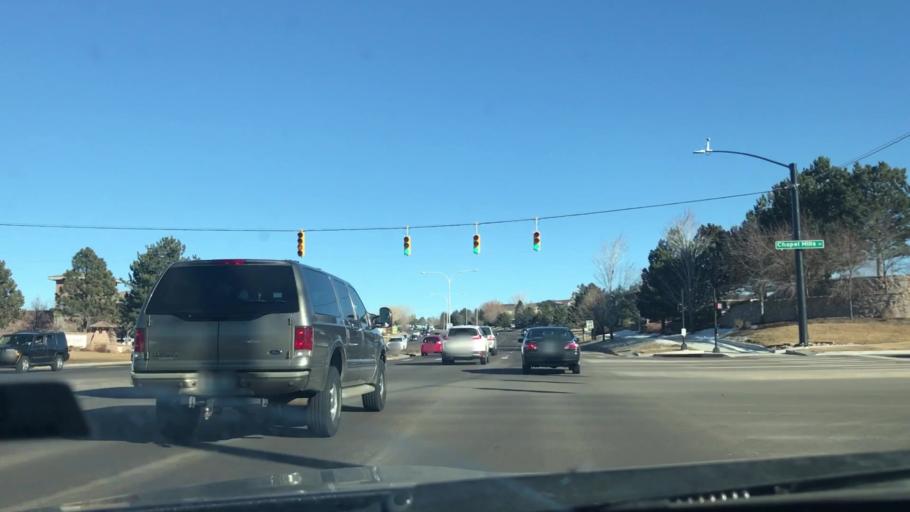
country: US
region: Colorado
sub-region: El Paso County
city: Air Force Academy
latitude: 38.9666
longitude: -104.7849
